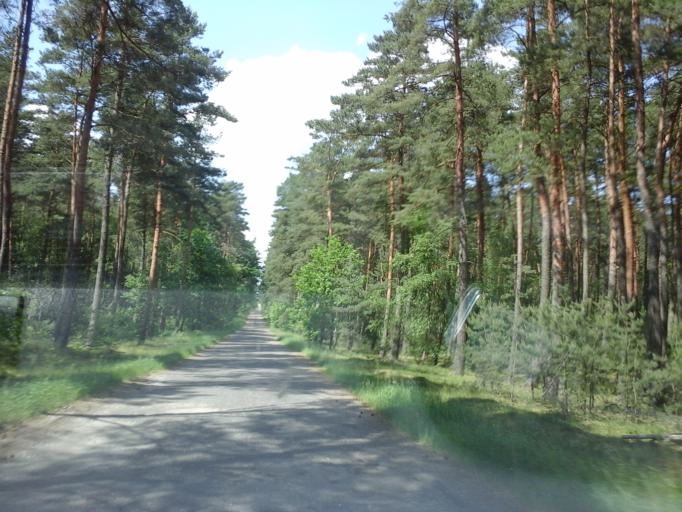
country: PL
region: West Pomeranian Voivodeship
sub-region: Powiat choszczenski
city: Drawno
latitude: 53.1358
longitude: 15.7164
